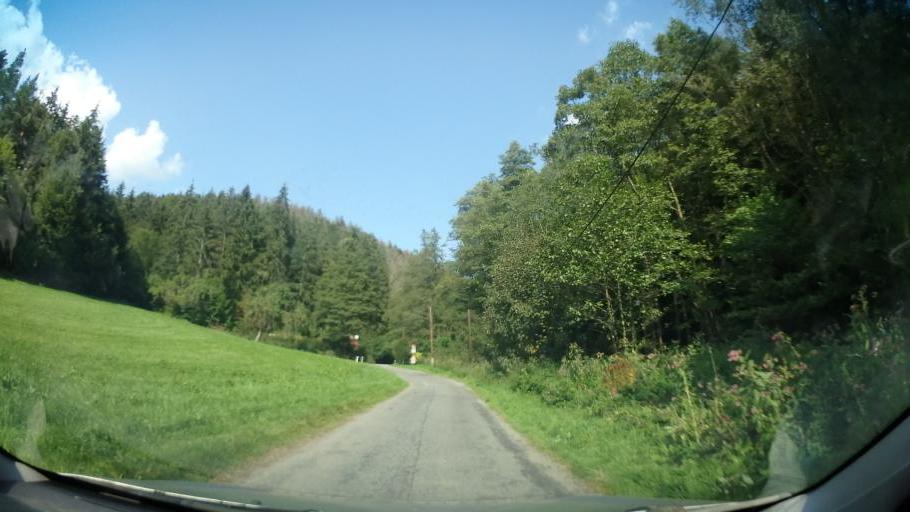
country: CZ
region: South Moravian
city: Olesnice
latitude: 49.5343
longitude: 16.3549
